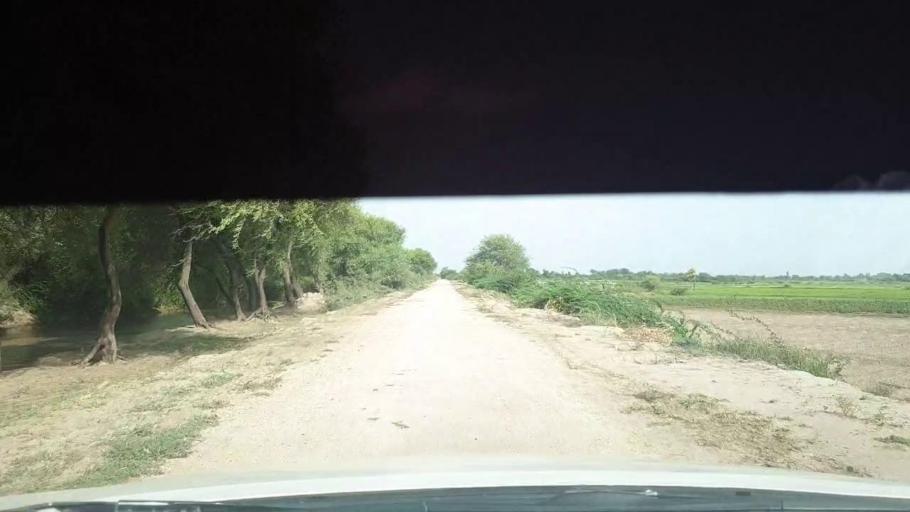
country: PK
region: Sindh
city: Kadhan
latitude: 24.5185
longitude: 69.0057
